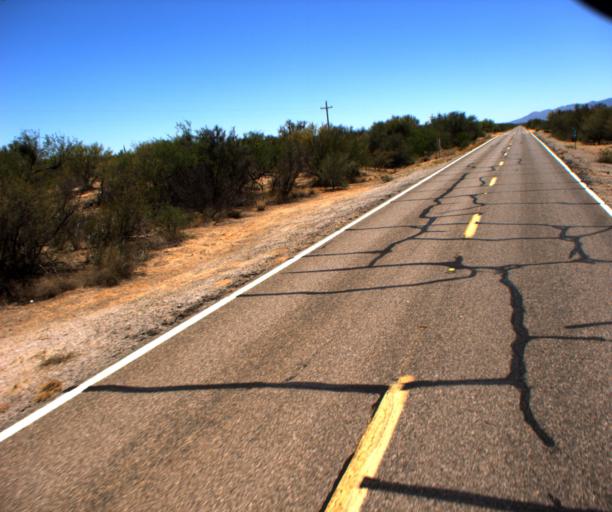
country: US
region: Arizona
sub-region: Pima County
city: Three Points
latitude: 31.9952
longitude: -111.3656
